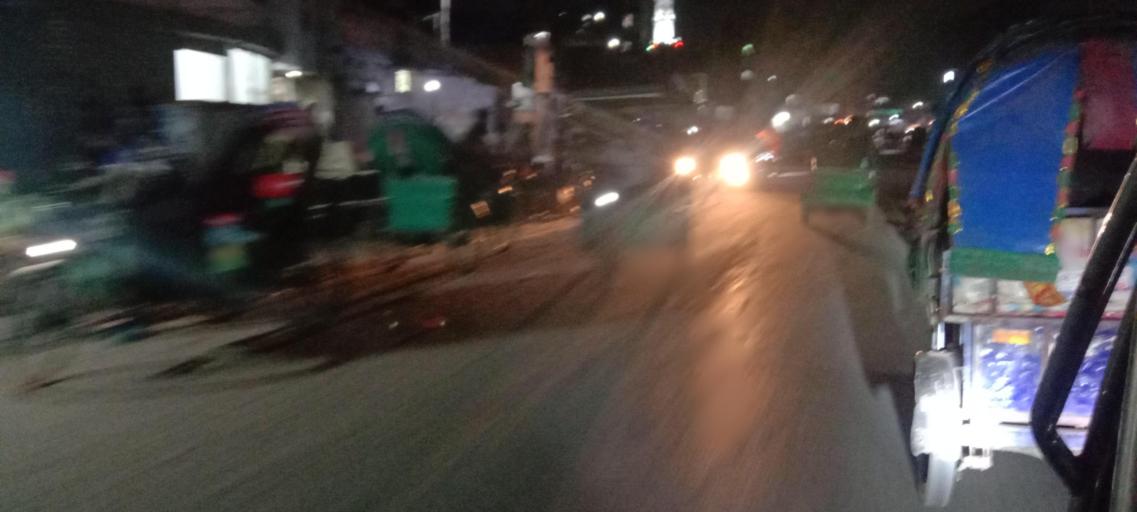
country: BD
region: Dhaka
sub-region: Dhaka
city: Dhaka
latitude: 23.7015
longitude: 90.3921
